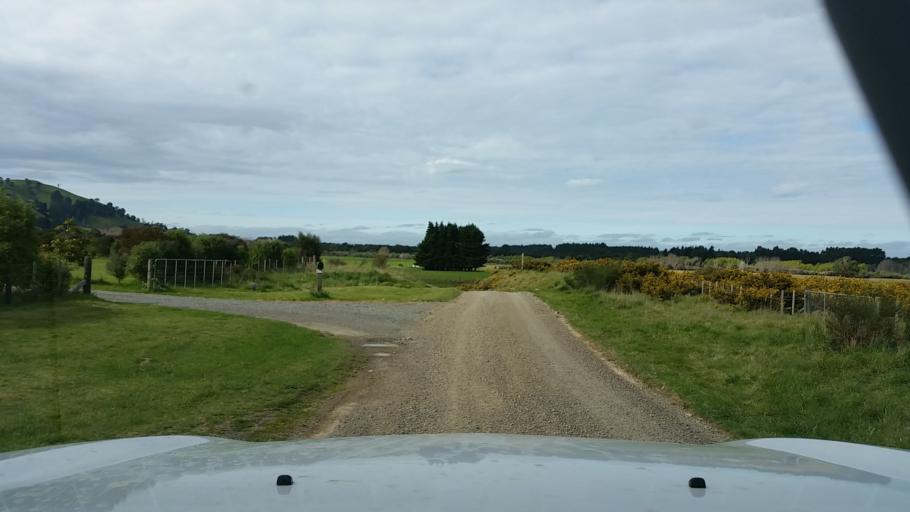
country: NZ
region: Wellington
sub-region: Upper Hutt City
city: Upper Hutt
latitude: -41.0831
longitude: 175.3554
